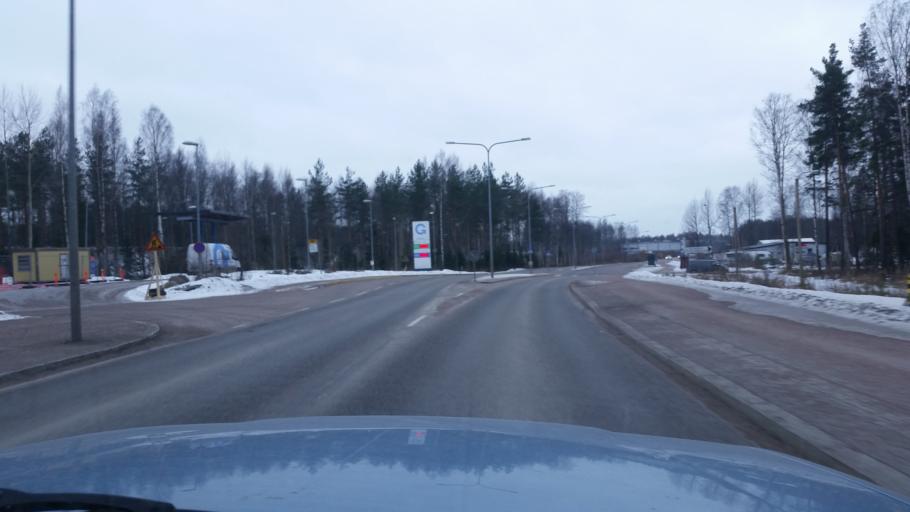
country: FI
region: Uusimaa
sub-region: Helsinki
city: Vantaa
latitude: 60.2536
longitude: 25.0632
